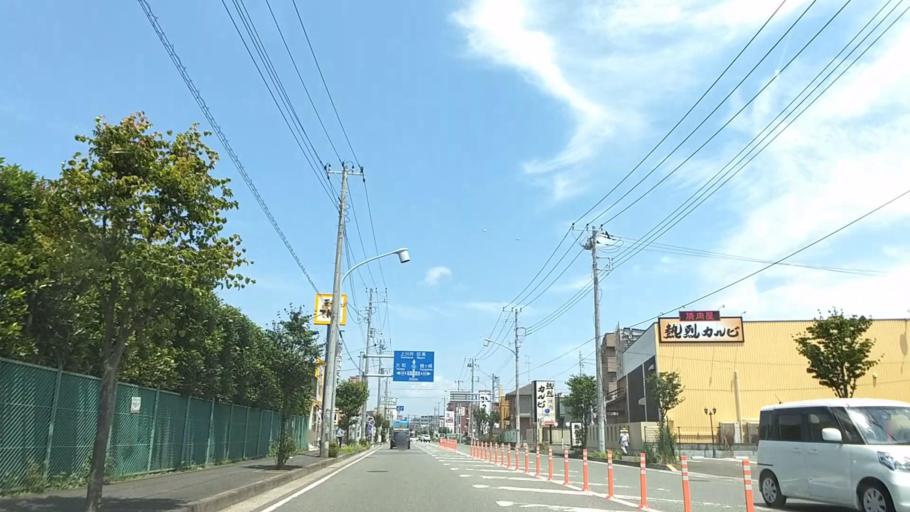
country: JP
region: Kanagawa
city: Minami-rinkan
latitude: 35.4627
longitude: 139.4802
